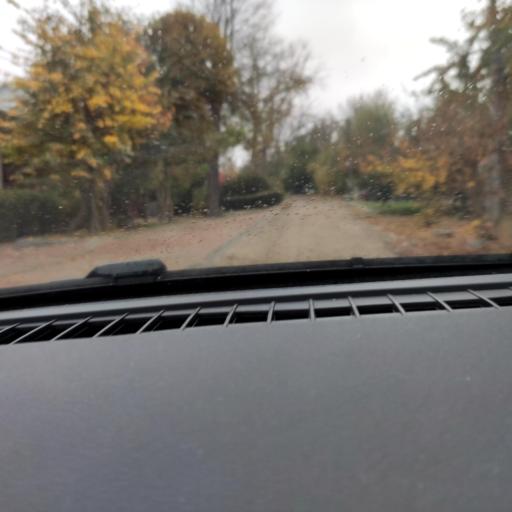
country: RU
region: Voronezj
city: Voronezh
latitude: 51.6967
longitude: 39.2152
